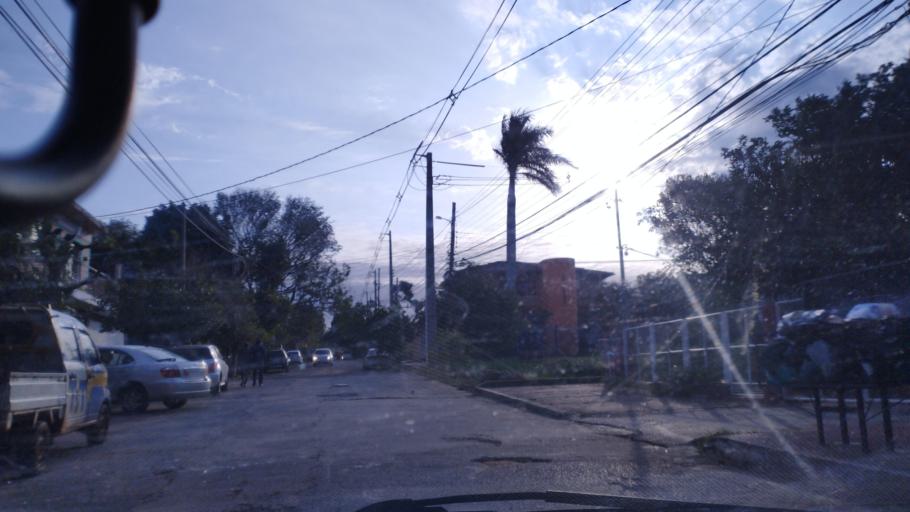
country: PY
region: Central
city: Fernando de la Mora
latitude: -25.3091
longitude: -57.5336
